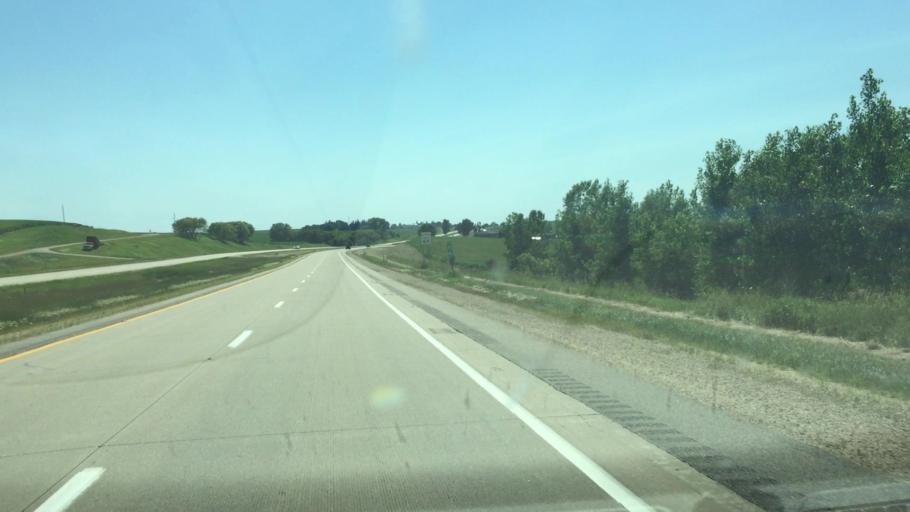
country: US
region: Iowa
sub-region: Dubuque County
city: Peosta
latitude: 42.3496
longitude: -90.8313
